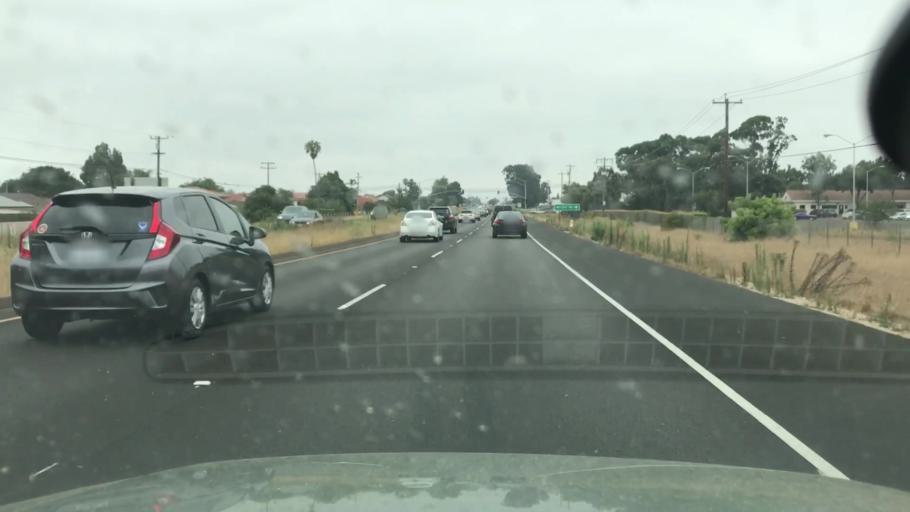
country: US
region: California
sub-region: Santa Barbara County
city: Orcutt
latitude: 34.9068
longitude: -120.4358
